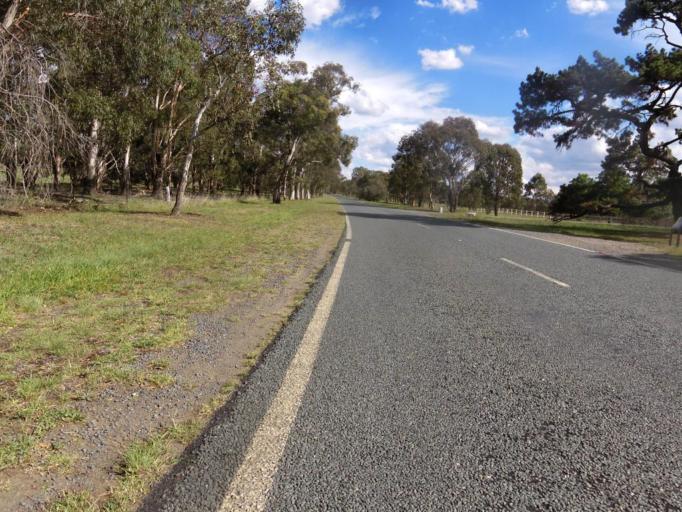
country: AU
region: Australian Capital Territory
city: Belconnen
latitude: -35.1754
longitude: 149.0714
